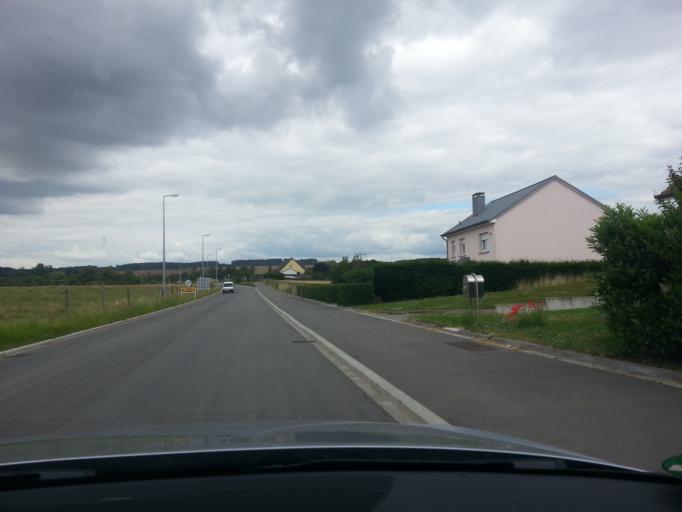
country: LU
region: Grevenmacher
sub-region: Canton de Remich
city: Mondorf-les-Bains
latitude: 49.5166
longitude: 6.3035
